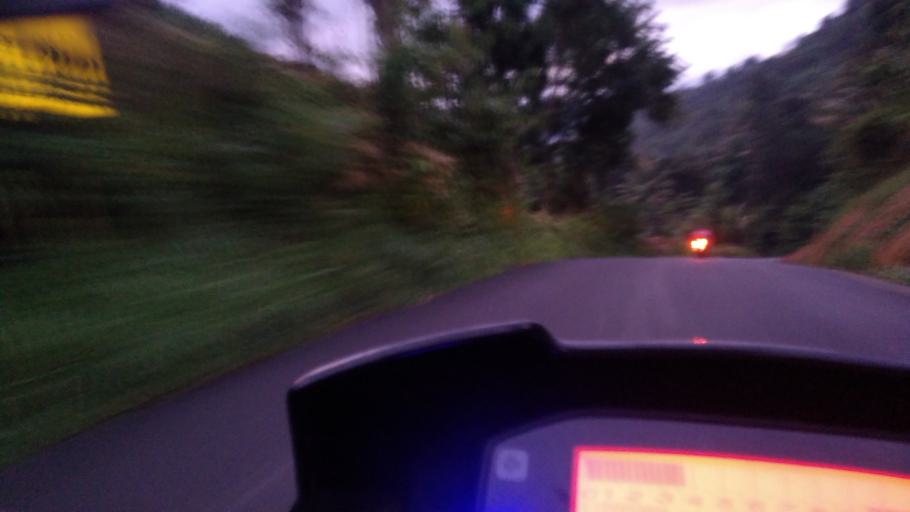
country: IN
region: Kerala
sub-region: Idukki
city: Munnar
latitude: 9.9663
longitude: 77.0638
